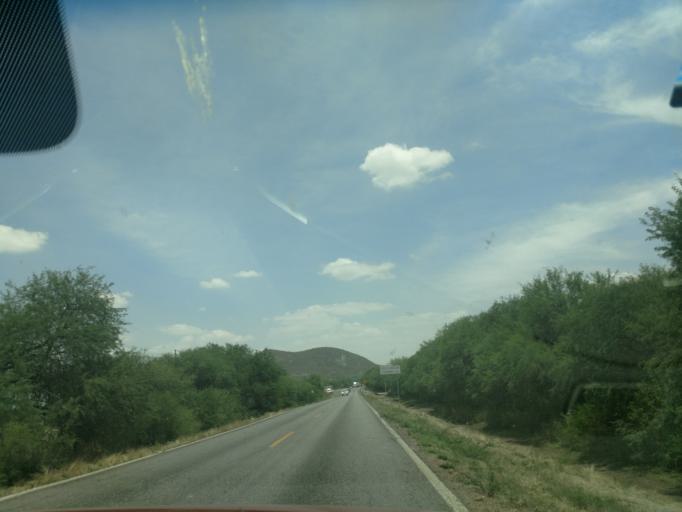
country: MX
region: San Luis Potosi
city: Ciudad Fernandez
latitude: 22.0070
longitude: -100.1503
